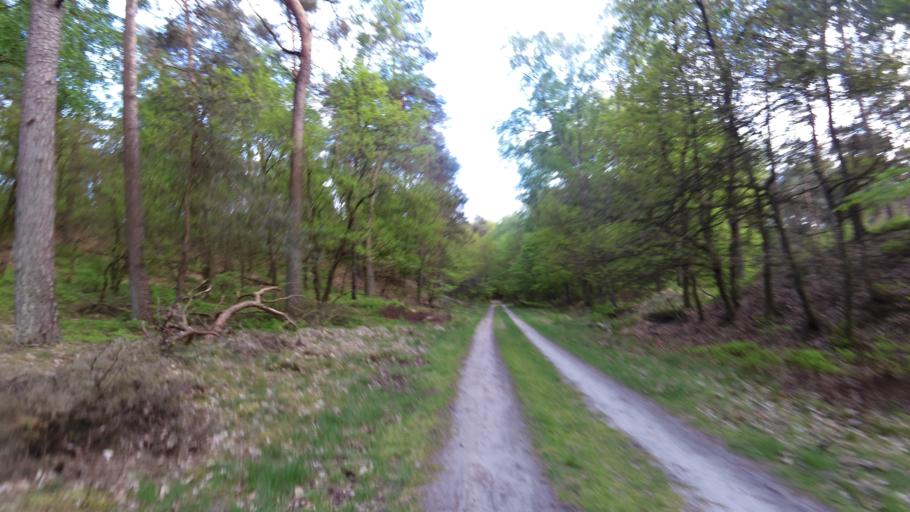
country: NL
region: Gelderland
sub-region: Gemeente Rozendaal
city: Rozendaal
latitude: 52.0245
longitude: 5.9591
